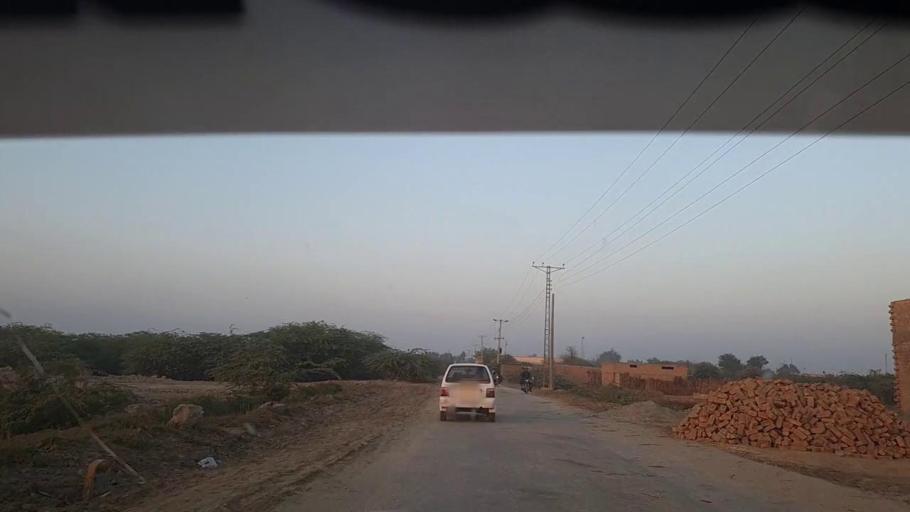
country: PK
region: Sindh
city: Ranipur
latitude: 27.2757
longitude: 68.5138
